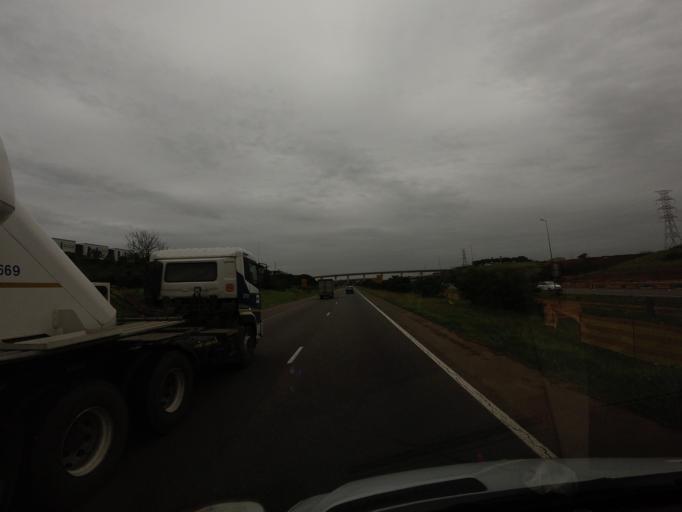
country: ZA
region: KwaZulu-Natal
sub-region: eThekwini Metropolitan Municipality
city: Durban
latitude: -29.7163
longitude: 31.0629
